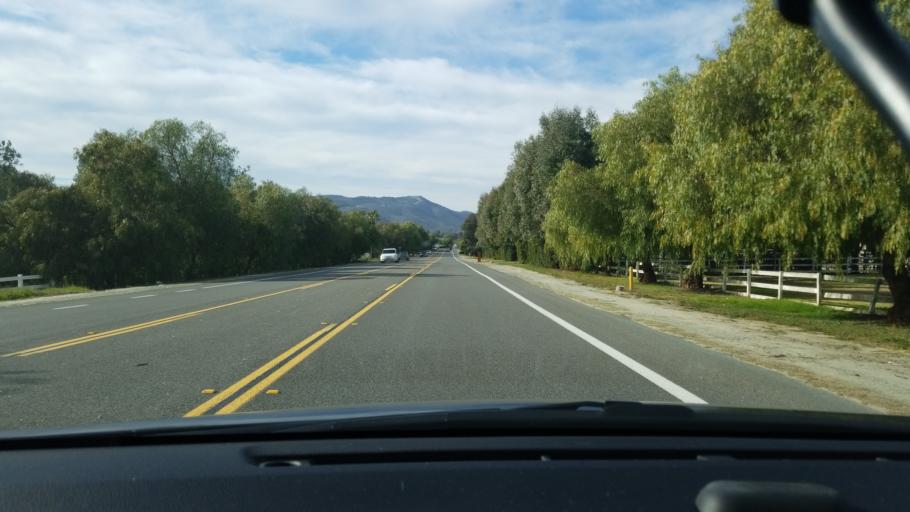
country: US
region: California
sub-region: Riverside County
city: Temecula
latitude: 33.4789
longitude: -117.1257
